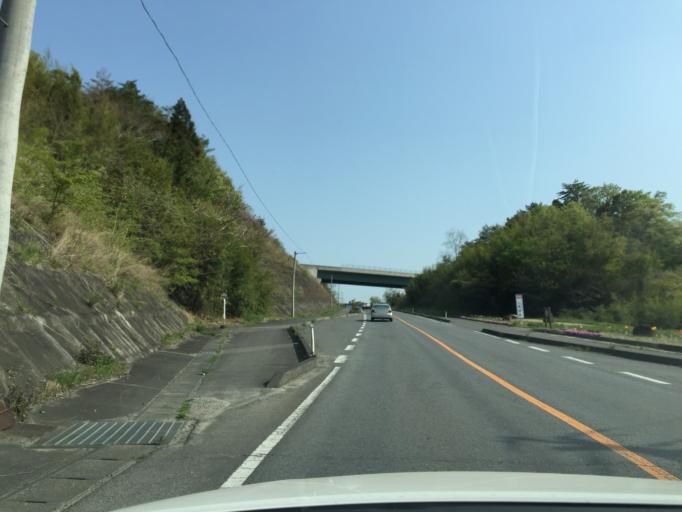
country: JP
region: Fukushima
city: Iwaki
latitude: 37.1063
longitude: 140.8756
